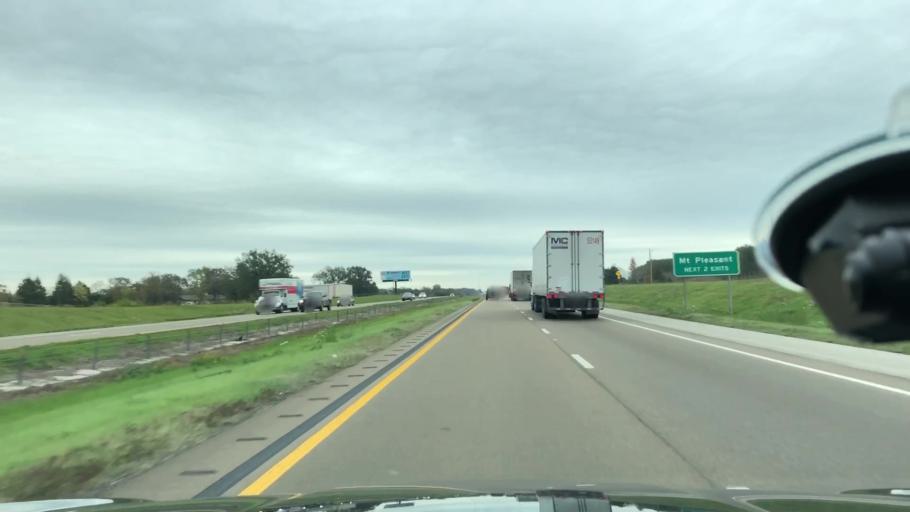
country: US
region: Texas
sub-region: Titus County
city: Mount Pleasant
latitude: 33.1620
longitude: -95.0250
